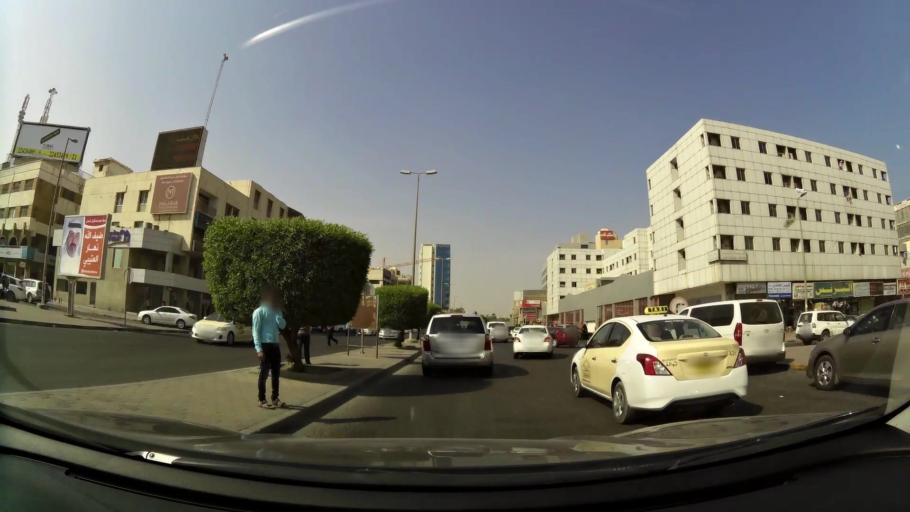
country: KW
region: Al Ahmadi
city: Al Fahahil
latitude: 29.0788
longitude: 48.1355
